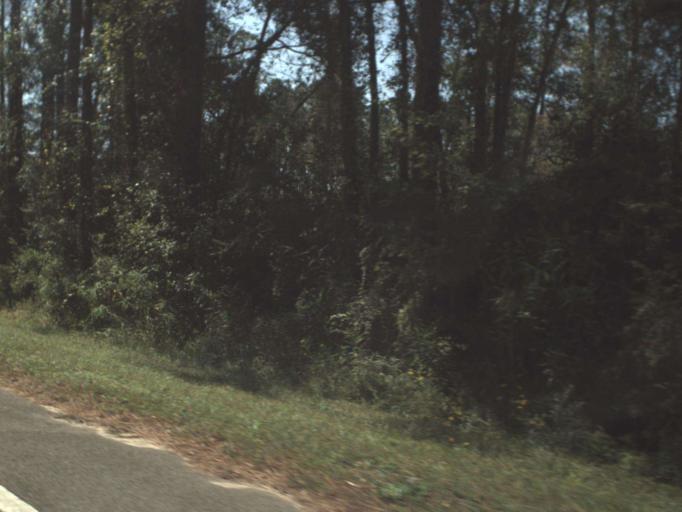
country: US
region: Florida
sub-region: Walton County
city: DeFuniak Springs
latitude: 30.9241
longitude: -86.1369
